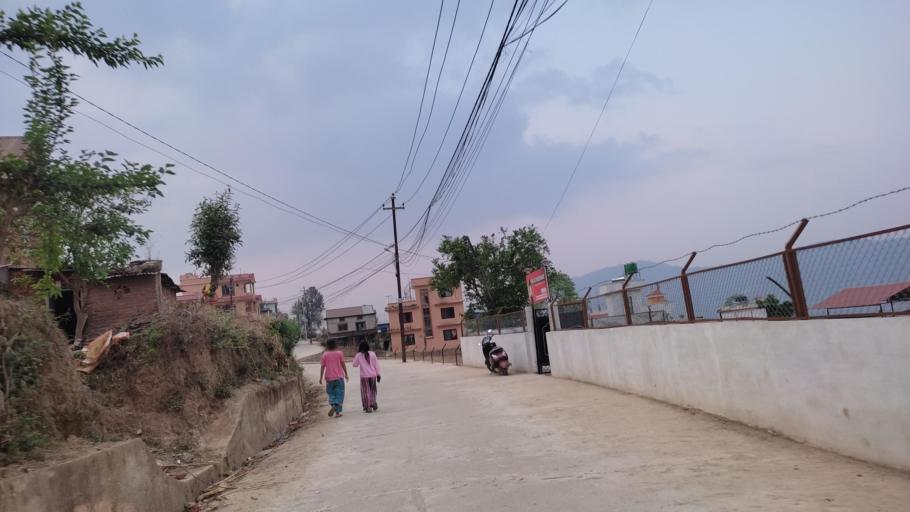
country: NP
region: Central Region
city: Kirtipur
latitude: 27.6691
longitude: 85.2457
